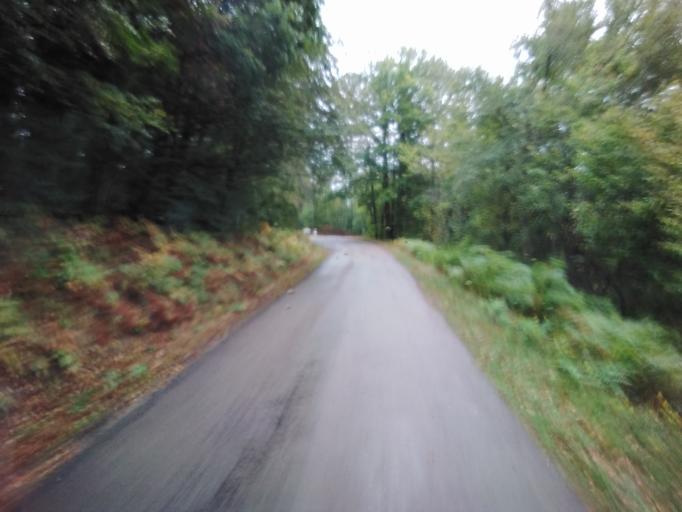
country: FR
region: Bourgogne
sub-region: Departement de la Nievre
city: Lormes
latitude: 47.2900
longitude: 3.9794
